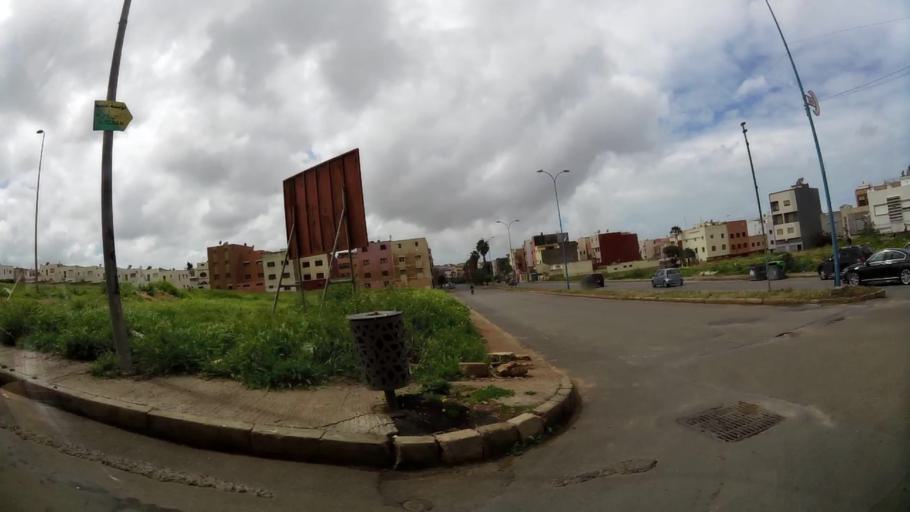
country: MA
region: Grand Casablanca
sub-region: Casablanca
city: Casablanca
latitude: 33.5337
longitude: -7.5979
